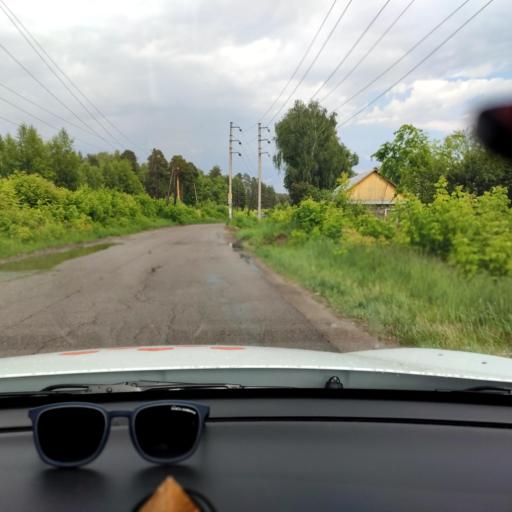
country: RU
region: Tatarstan
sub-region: Zelenodol'skiy Rayon
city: Vasil'yevo
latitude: 55.8367
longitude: 48.6869
